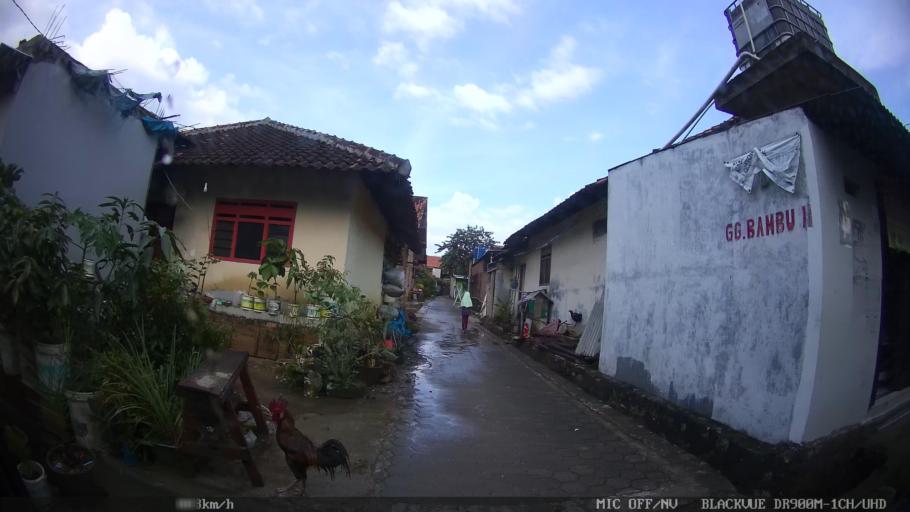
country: ID
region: Lampung
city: Kedaton
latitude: -5.3899
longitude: 105.2966
